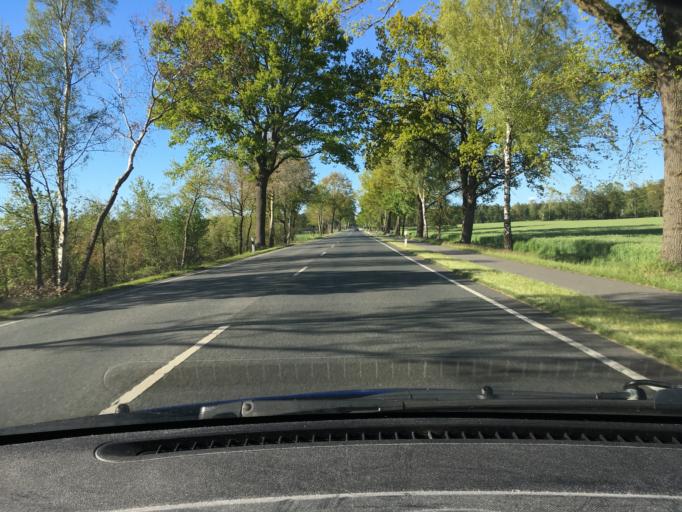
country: DE
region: Lower Saxony
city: Soltau
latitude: 53.0310
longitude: 9.8520
